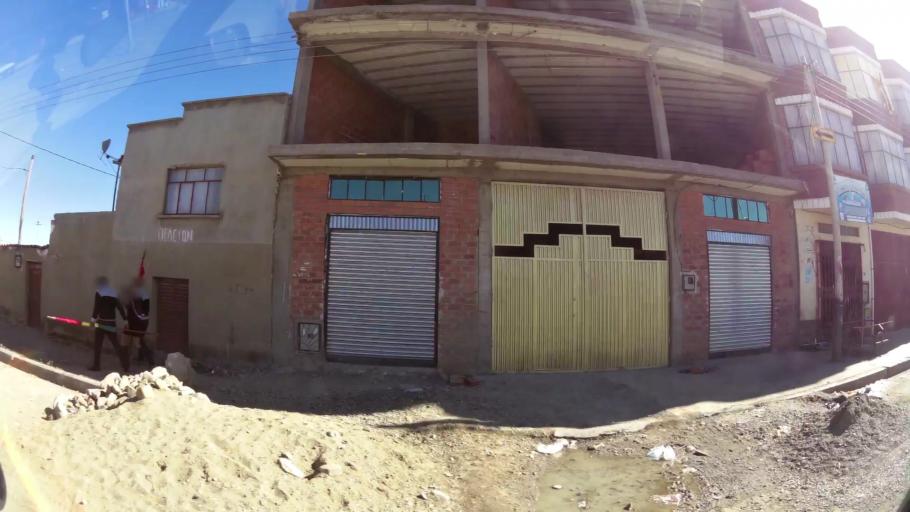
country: BO
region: La Paz
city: La Paz
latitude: -16.5310
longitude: -68.2213
